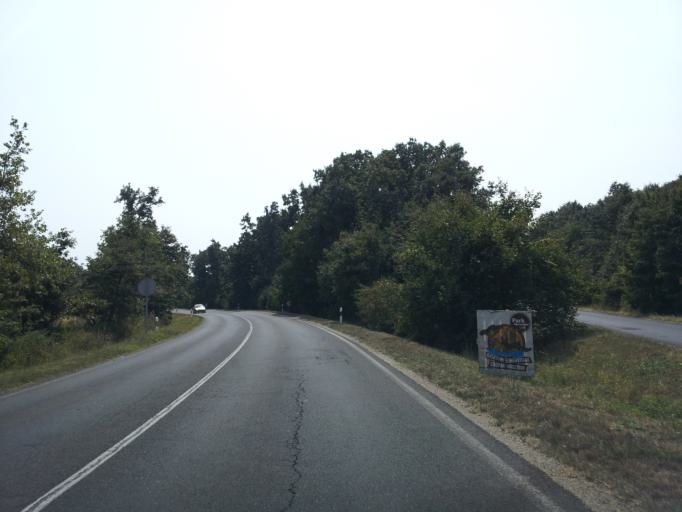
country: HU
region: Veszprem
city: Nemesvamos
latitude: 47.0243
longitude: 17.9068
